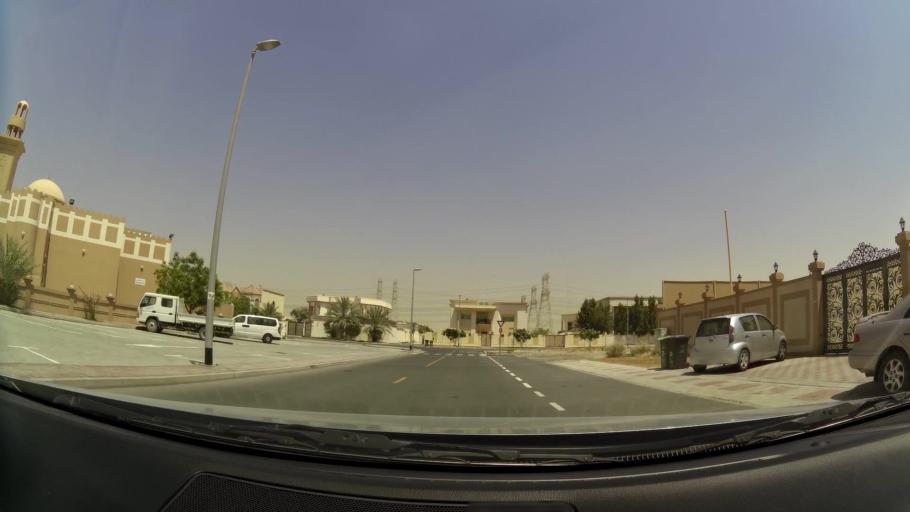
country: AE
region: Dubai
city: Dubai
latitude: 25.0971
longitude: 55.2208
